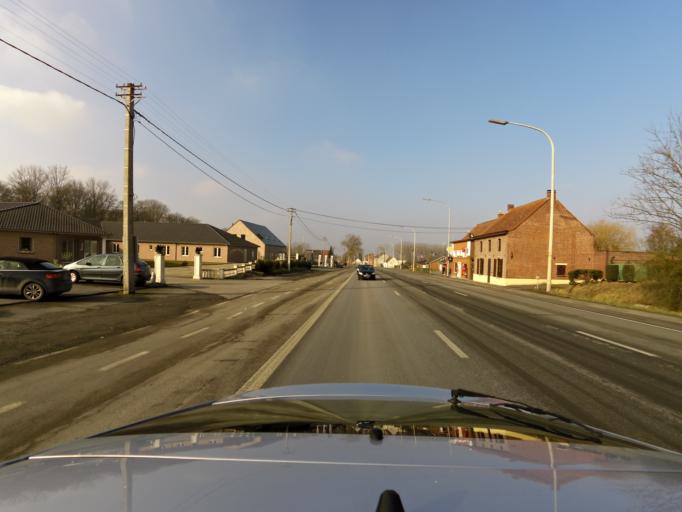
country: BE
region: Wallonia
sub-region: Province du Hainaut
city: Antoing
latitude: 50.5958
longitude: 3.5084
